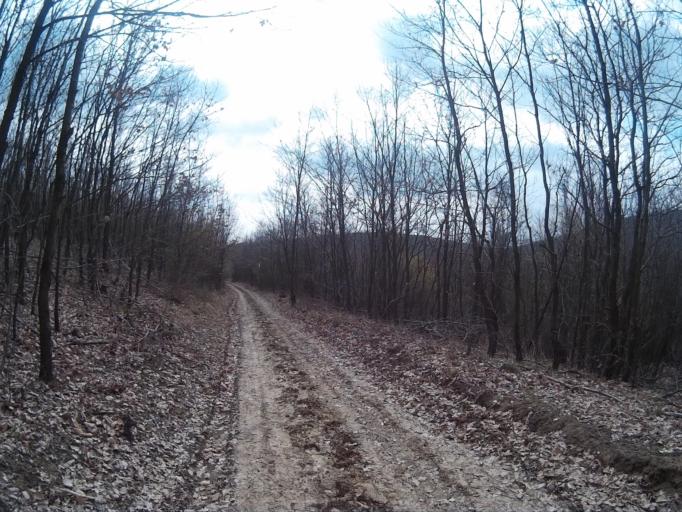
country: HU
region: Pest
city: Kosd
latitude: 47.8411
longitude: 19.1808
